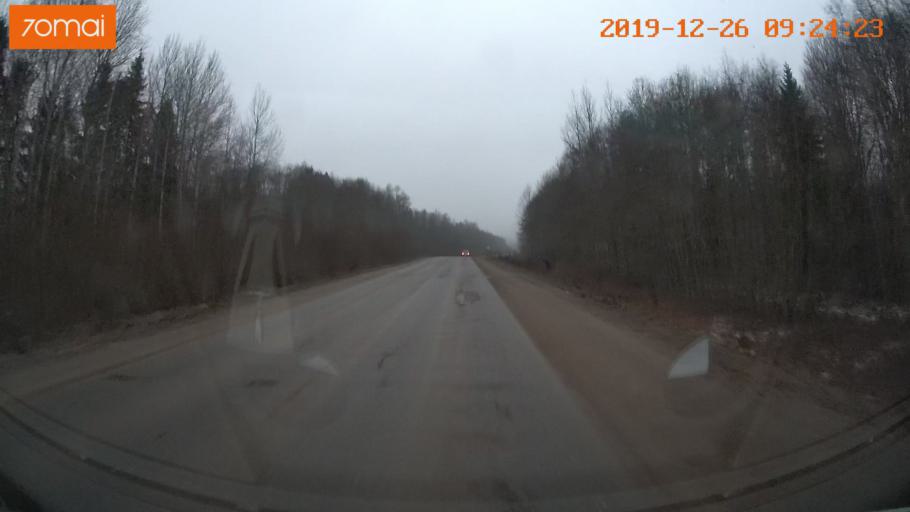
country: RU
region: Vologda
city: Gryazovets
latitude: 59.0000
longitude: 40.1991
